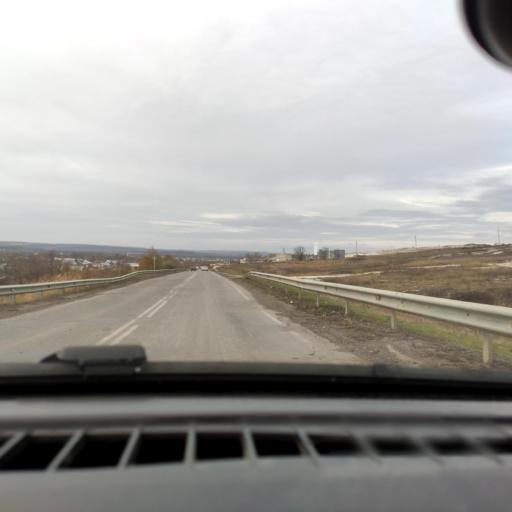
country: RU
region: Belgorod
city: Alekseyevka
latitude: 50.6406
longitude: 38.6771
